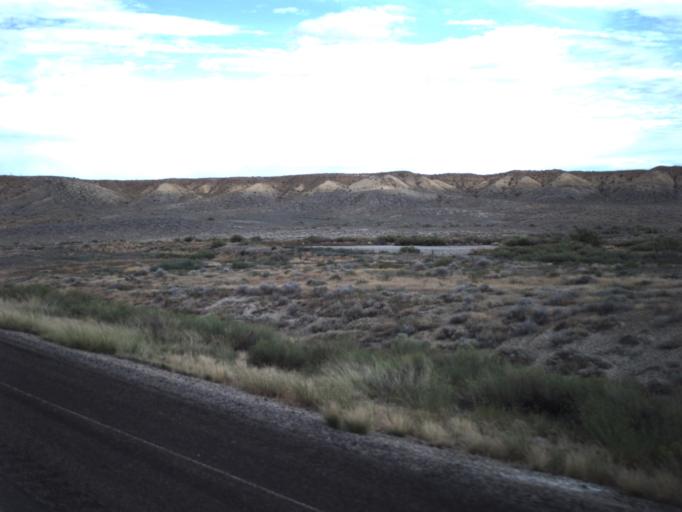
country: US
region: Utah
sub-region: Grand County
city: Moab
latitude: 38.9499
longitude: -109.6802
